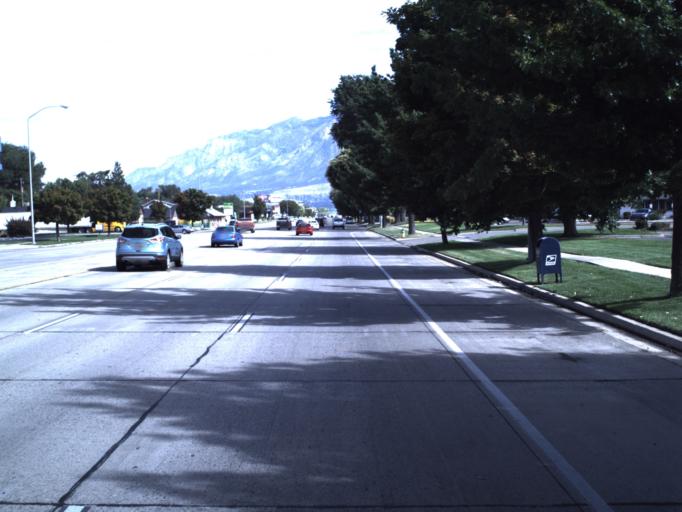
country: US
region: Utah
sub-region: Weber County
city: Ogden
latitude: 41.2462
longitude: -111.9698
